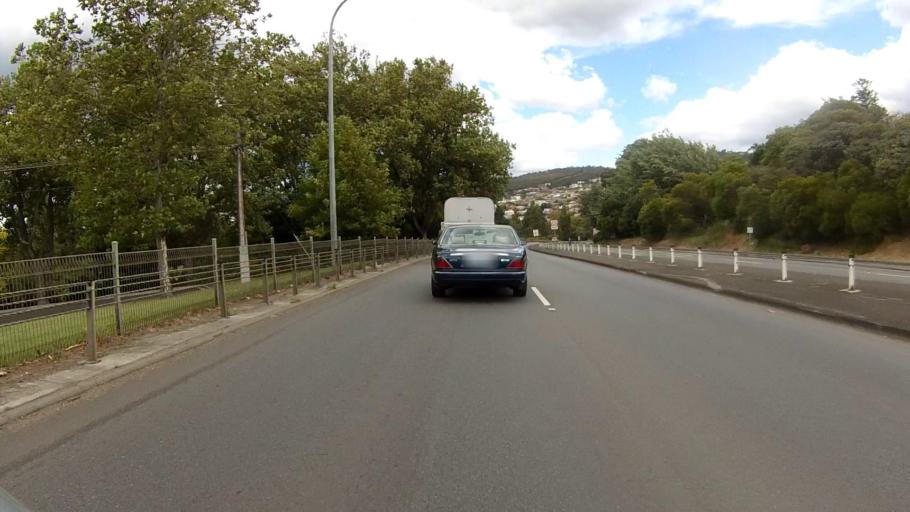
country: AU
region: Tasmania
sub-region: Hobart
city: Sandy Bay
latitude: -42.8932
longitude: 147.3184
